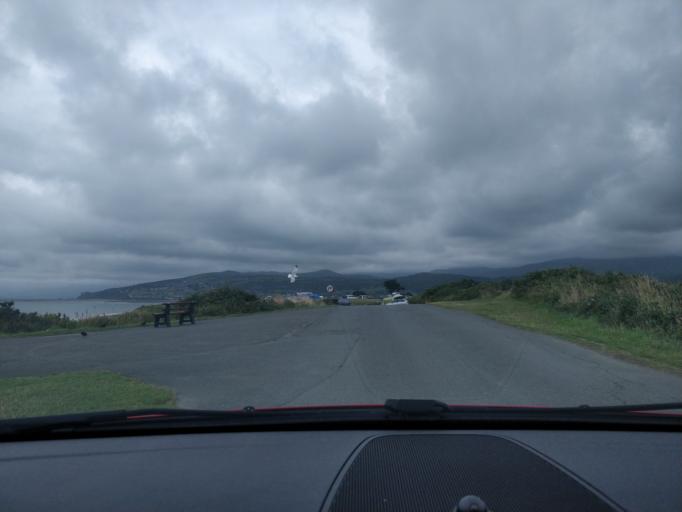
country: GB
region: Wales
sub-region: Gwynedd
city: Llanfair
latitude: 52.8173
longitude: -4.1474
